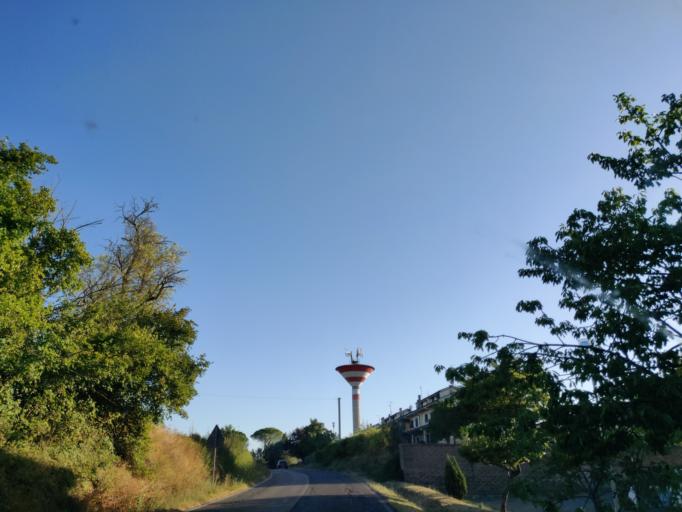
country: IT
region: Latium
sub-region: Provincia di Viterbo
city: Acquapendente
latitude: 42.7381
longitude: 11.8776
